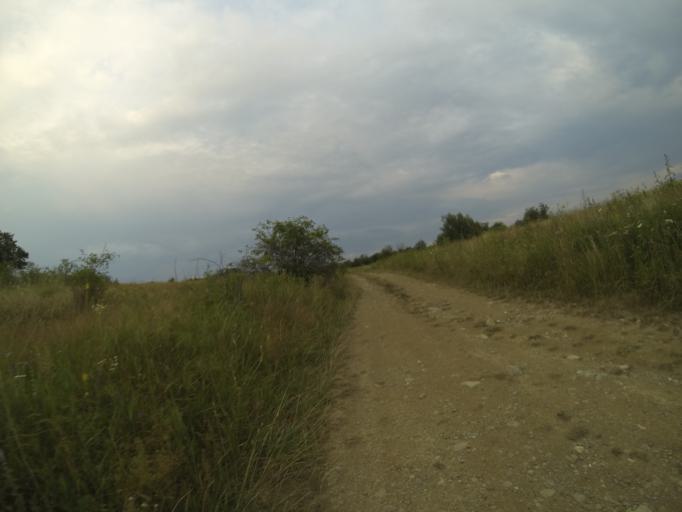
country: RO
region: Brasov
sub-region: Comuna Sinca Veche
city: Sinca Veche
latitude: 45.7759
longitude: 25.1644
